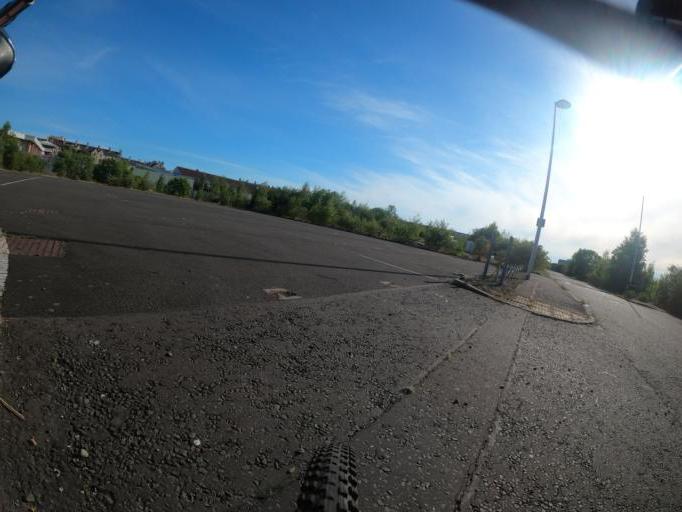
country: GB
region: Scotland
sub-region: Edinburgh
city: Edinburgh
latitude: 55.9802
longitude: -3.2335
